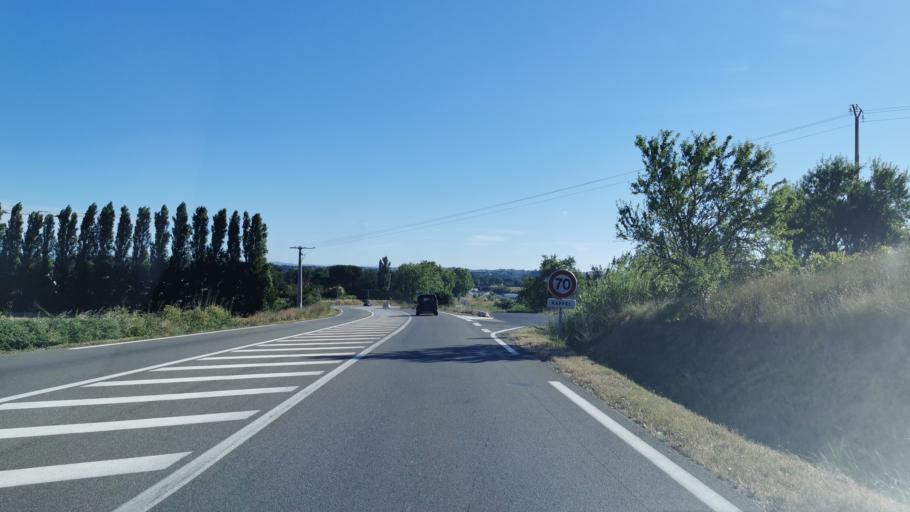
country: FR
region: Languedoc-Roussillon
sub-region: Departement de l'Herault
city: Beziers
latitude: 43.3197
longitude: 3.1857
